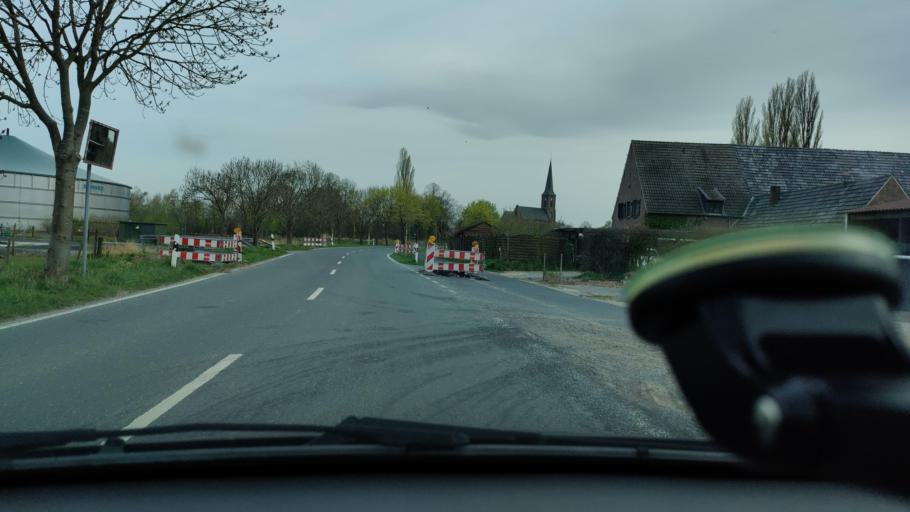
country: DE
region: North Rhine-Westphalia
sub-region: Regierungsbezirk Dusseldorf
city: Kleve
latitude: 51.7809
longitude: 6.1780
